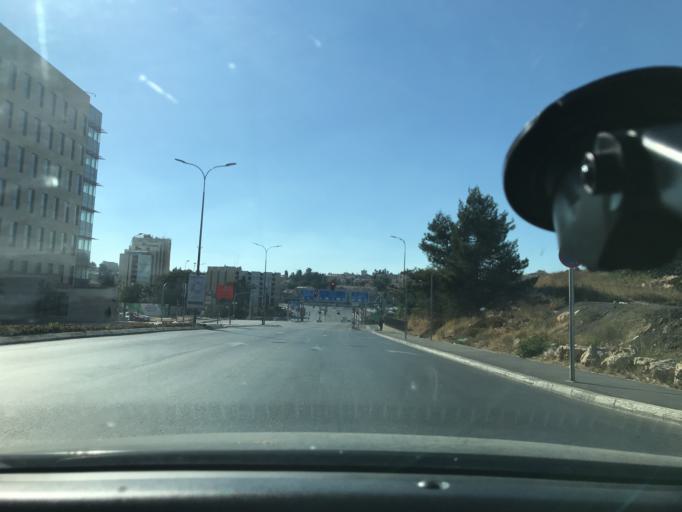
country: IL
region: Jerusalem
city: West Jerusalem
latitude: 31.7833
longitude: 35.2014
